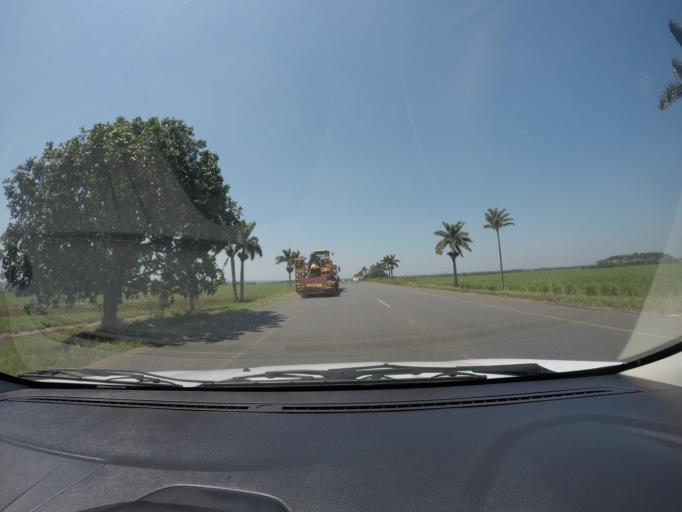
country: ZA
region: KwaZulu-Natal
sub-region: uThungulu District Municipality
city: Empangeni
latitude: -28.8100
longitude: 31.9561
